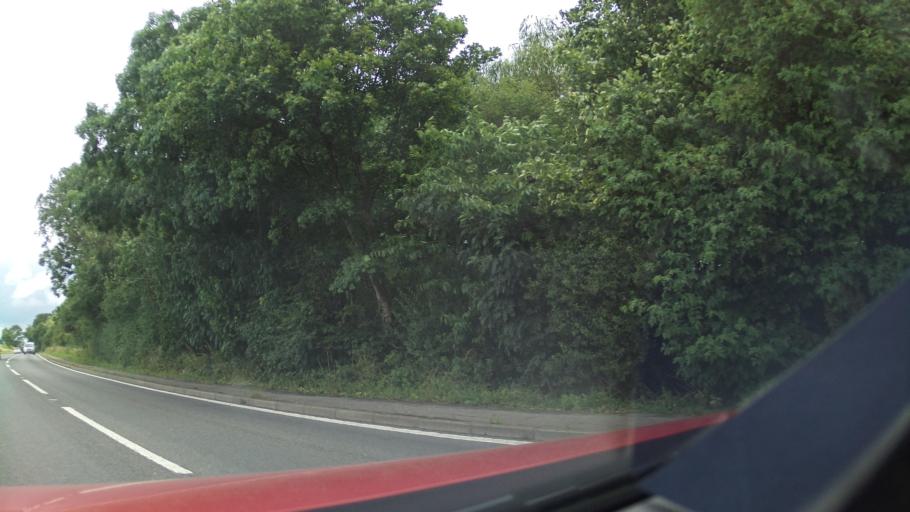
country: GB
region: England
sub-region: Northamptonshire
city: Corby
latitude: 52.4969
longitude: -0.7291
